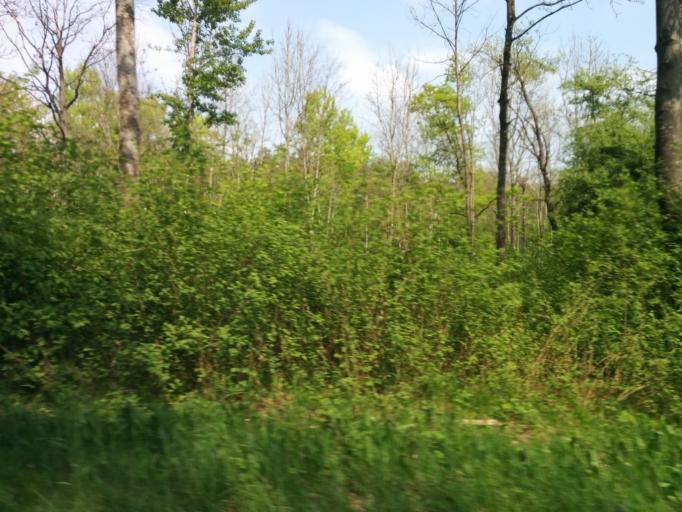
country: DE
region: Bavaria
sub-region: Lower Bavaria
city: Moos
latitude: 48.7732
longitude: 12.9600
